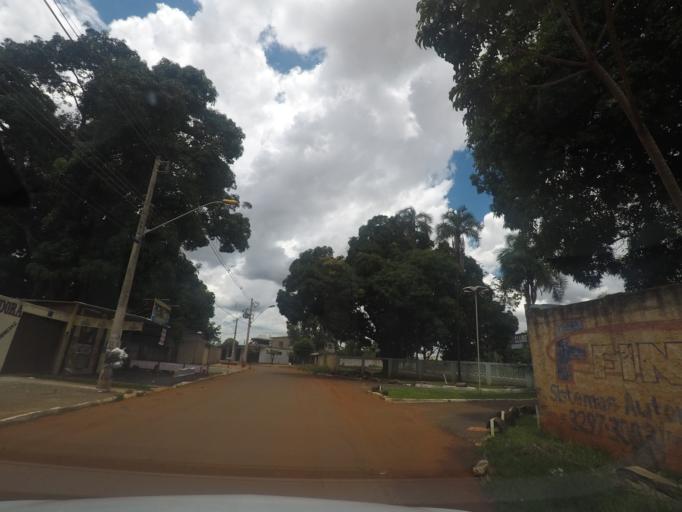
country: BR
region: Goias
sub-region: Goiania
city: Goiania
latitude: -16.7092
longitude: -49.3466
